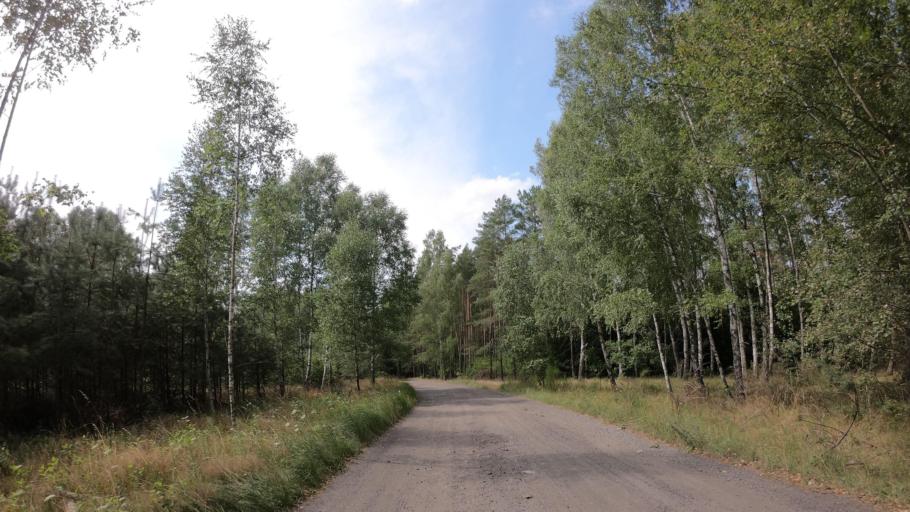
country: PL
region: West Pomeranian Voivodeship
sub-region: Powiat walecki
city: Tuczno
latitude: 53.2308
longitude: 16.0552
